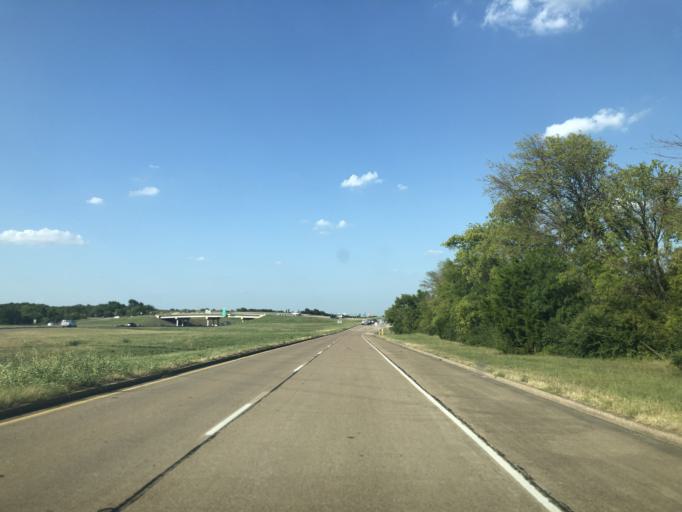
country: US
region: Texas
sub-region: Tarrant County
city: Sansom Park
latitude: 32.8269
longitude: -97.3816
